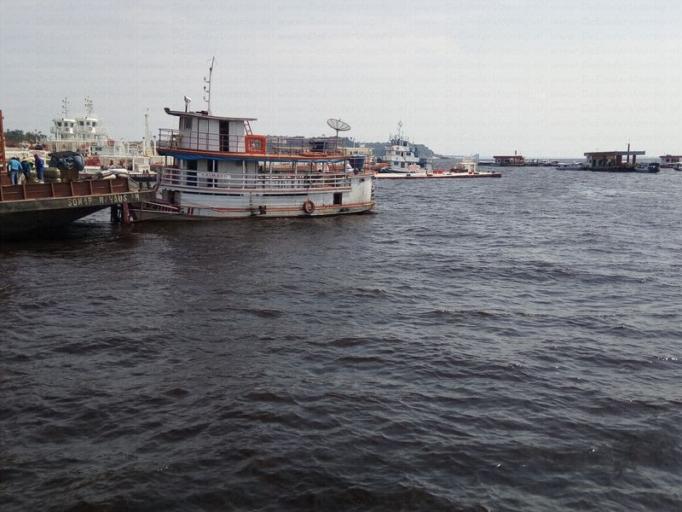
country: BR
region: Amazonas
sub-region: Manaus
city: Manaus
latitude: -3.1357
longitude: -59.9377
